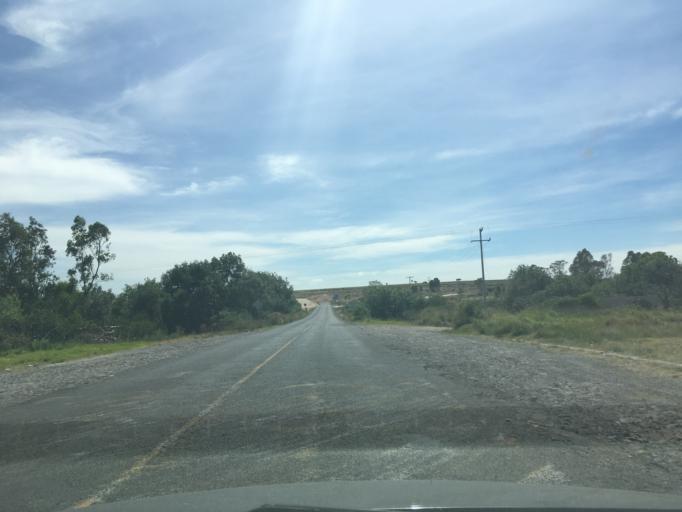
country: MX
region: Queretaro
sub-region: San Juan del Rio
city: El Jazmin
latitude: 20.2728
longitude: -100.0656
